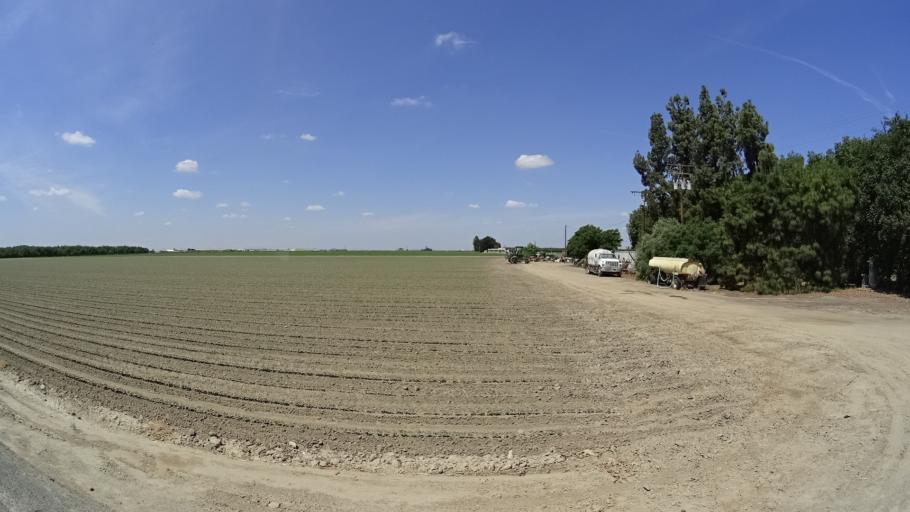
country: US
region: California
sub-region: Tulare County
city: Goshen
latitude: 36.3239
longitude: -119.4754
